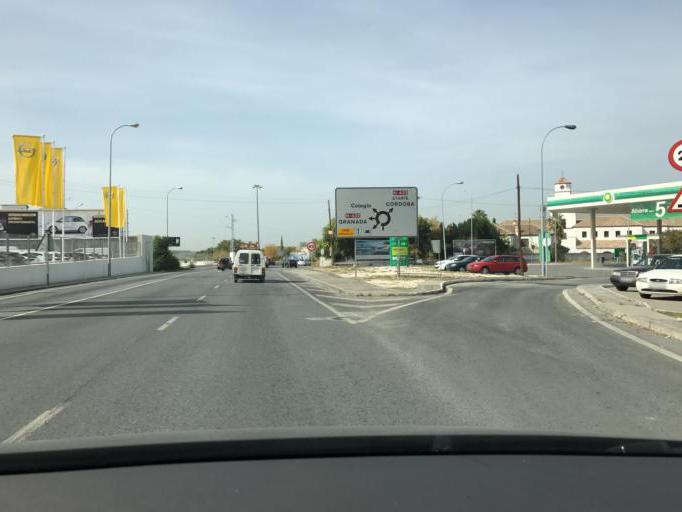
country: ES
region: Andalusia
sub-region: Provincia de Granada
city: Maracena
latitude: 37.1988
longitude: -3.6472
